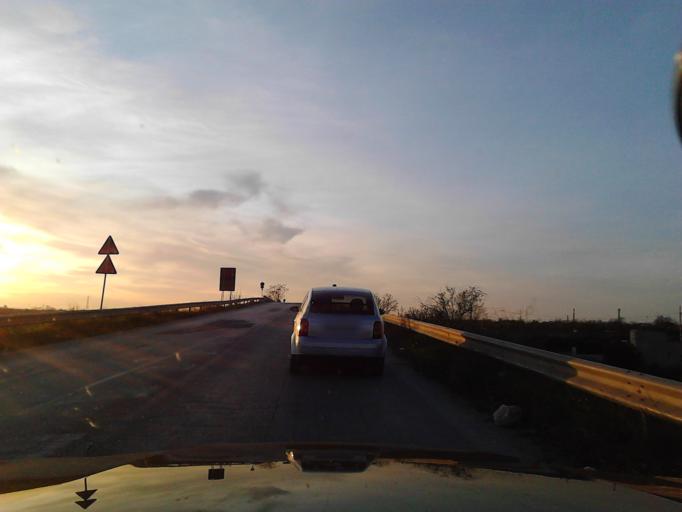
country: IT
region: Apulia
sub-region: Provincia di Bari
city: Triggiano
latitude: 41.0567
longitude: 16.9200
